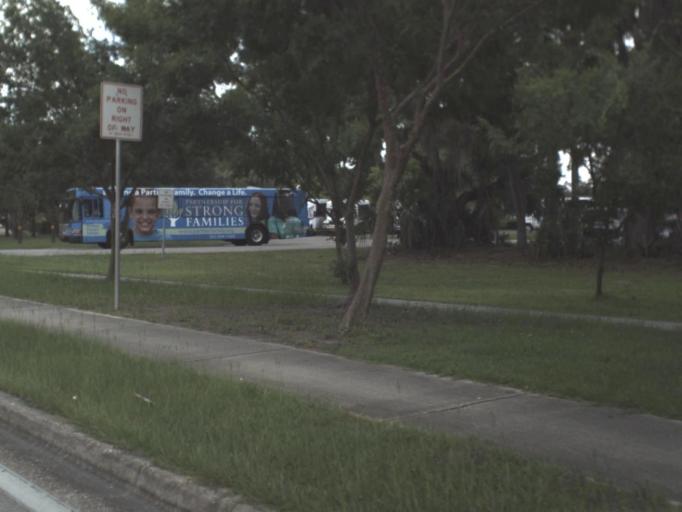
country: US
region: Florida
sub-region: Alachua County
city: Gainesville
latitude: 29.6360
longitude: -82.3520
